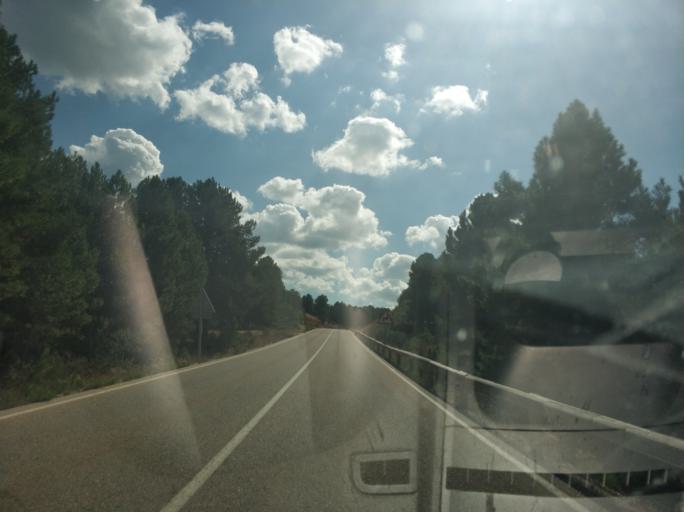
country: ES
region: Castille and Leon
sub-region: Provincia de Soria
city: Herrera de Soria
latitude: 41.7537
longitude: -3.0403
